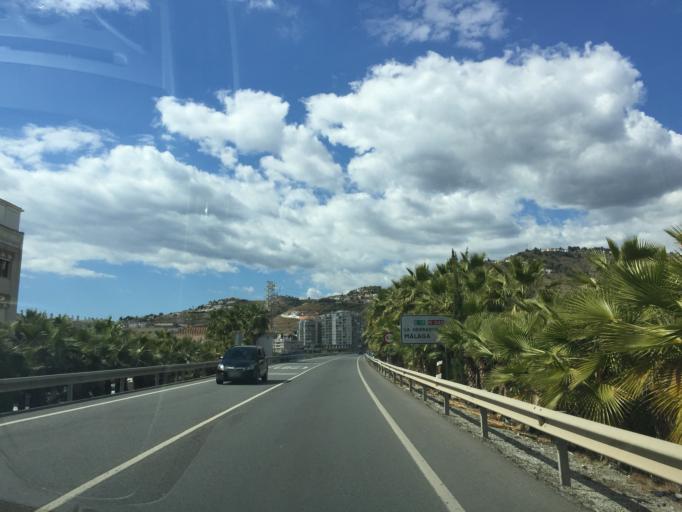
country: ES
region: Andalusia
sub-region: Provincia de Granada
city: Almunecar
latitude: 36.7376
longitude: -3.6904
